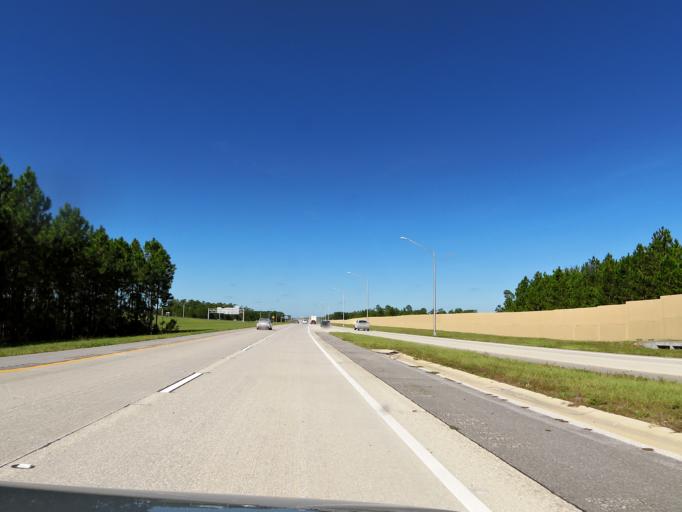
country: US
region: Florida
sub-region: Saint Johns County
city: Fruit Cove
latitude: 30.1183
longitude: -81.5131
